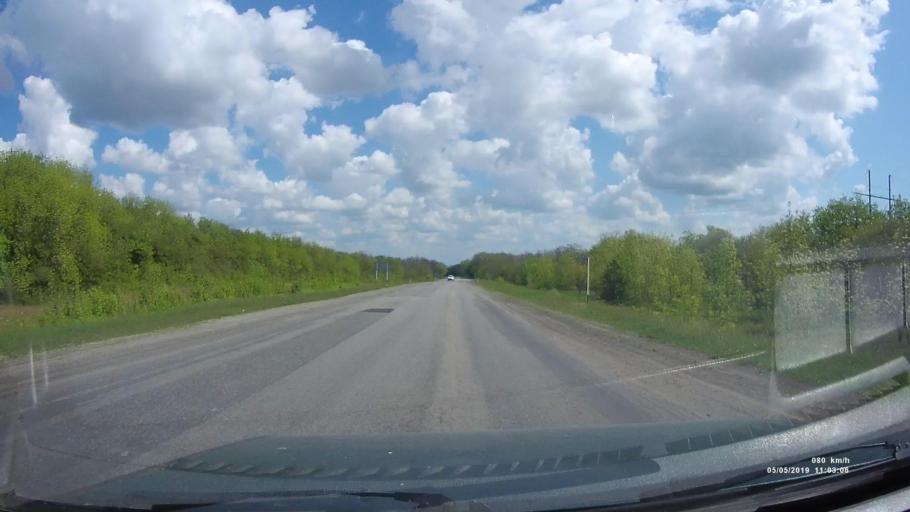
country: RU
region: Rostov
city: Ust'-Donetskiy
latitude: 47.6892
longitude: 40.9161
